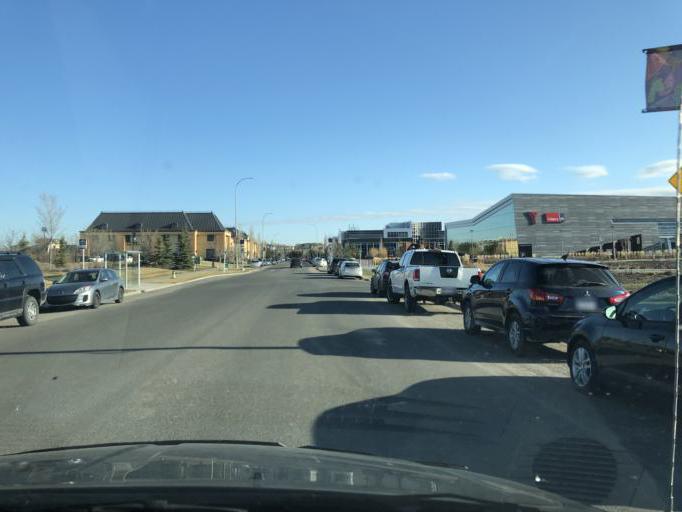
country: CA
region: Alberta
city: Calgary
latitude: 50.9603
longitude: -114.0072
